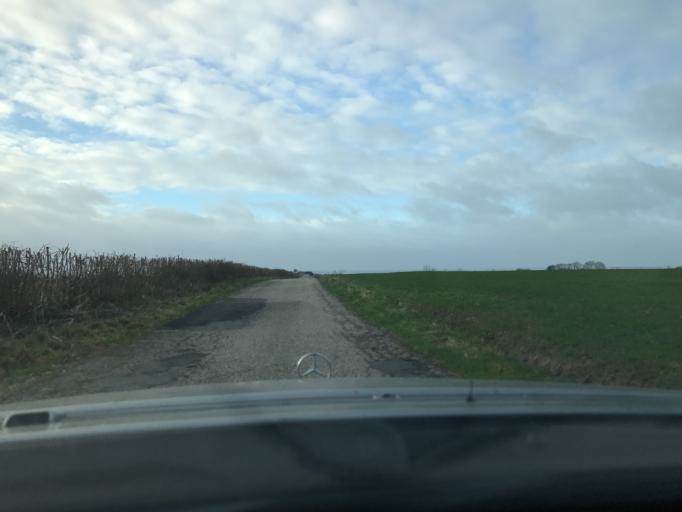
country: DK
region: South Denmark
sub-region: Sonderborg Kommune
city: Nordborg
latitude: 55.0497
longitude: 9.6770
